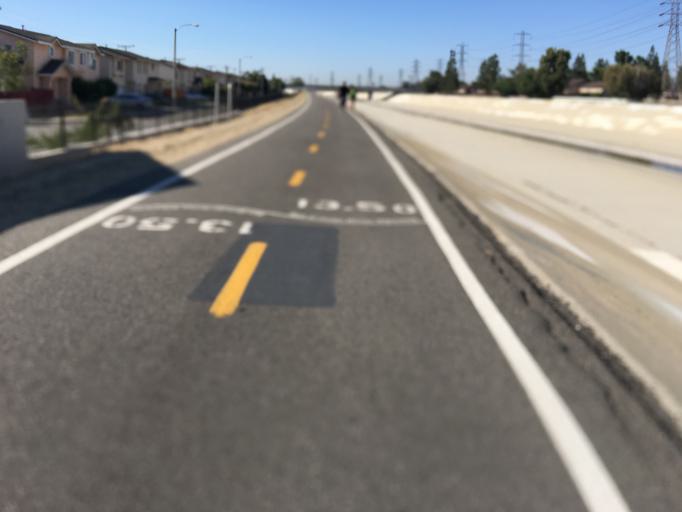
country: US
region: California
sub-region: Los Angeles County
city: Downey
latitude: 33.9208
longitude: -118.1112
